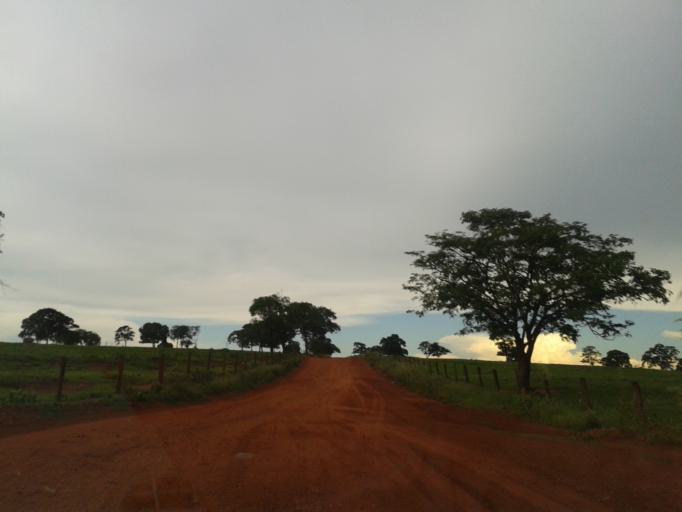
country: BR
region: Minas Gerais
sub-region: Santa Vitoria
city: Santa Vitoria
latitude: -19.1004
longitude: -50.5041
